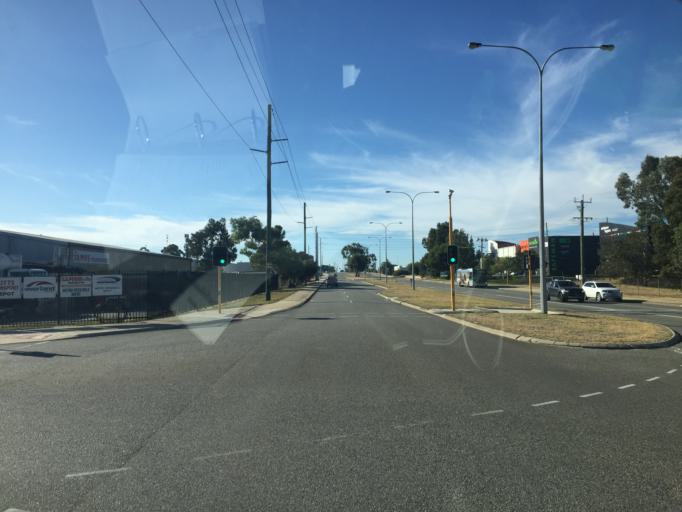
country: AU
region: Western Australia
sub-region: Belmont
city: Kewdale
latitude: -31.9776
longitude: 115.9538
